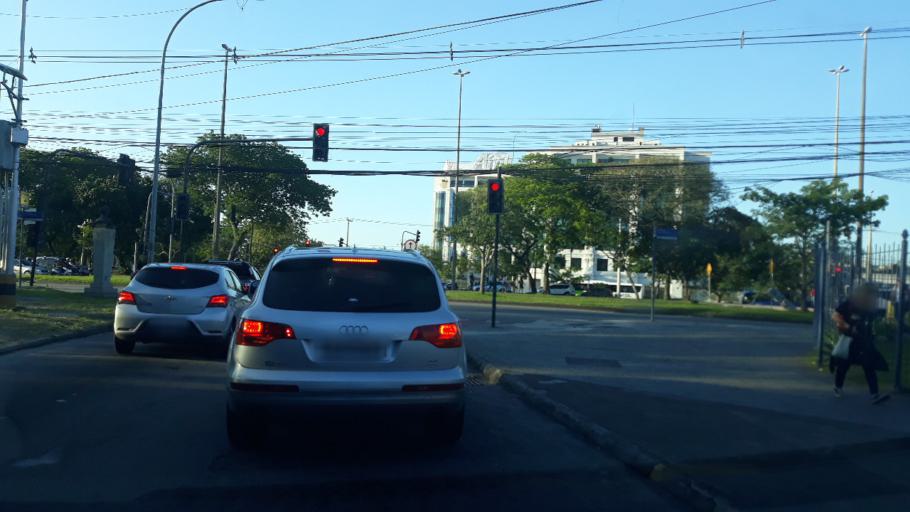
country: BR
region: Rio de Janeiro
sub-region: Rio De Janeiro
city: Rio de Janeiro
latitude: -23.0007
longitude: -43.3534
